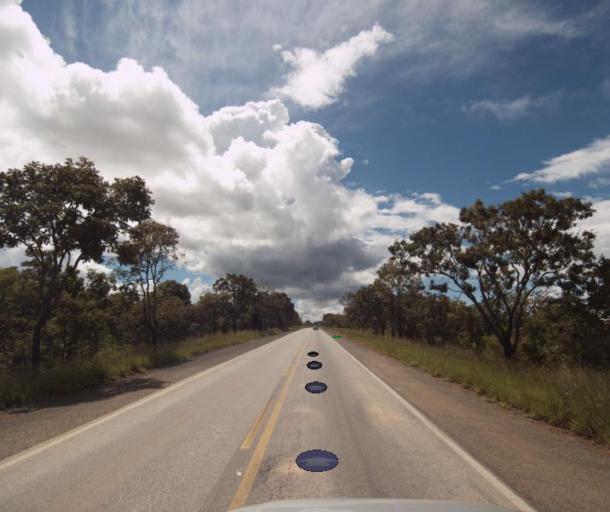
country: BR
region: Goias
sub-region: Uruacu
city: Uruacu
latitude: -14.0319
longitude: -49.0883
